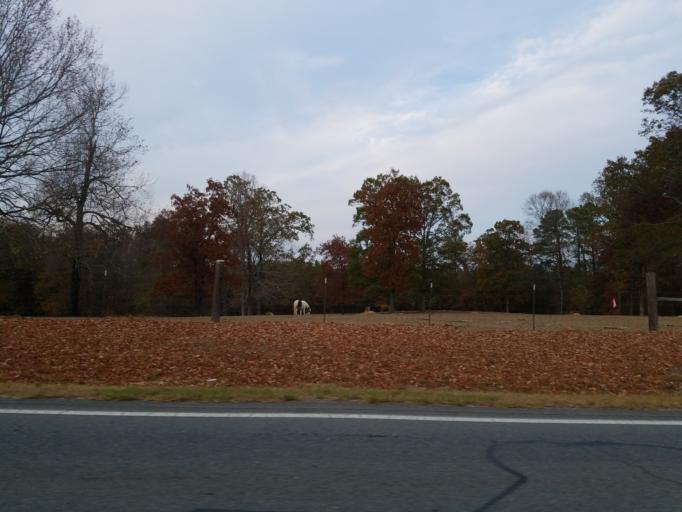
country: US
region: Georgia
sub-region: Gordon County
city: Calhoun
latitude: 34.6005
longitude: -84.8855
